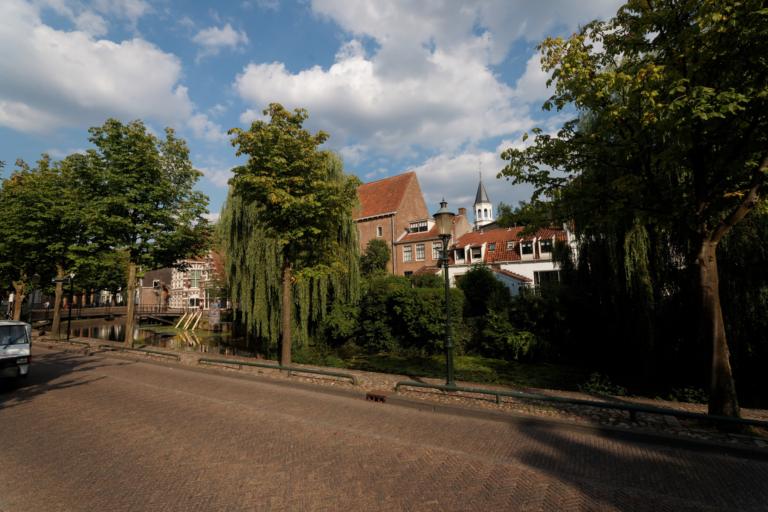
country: NL
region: Utrecht
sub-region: Gemeente Amersfoort
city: Amersfoort
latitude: 52.1573
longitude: 5.3856
